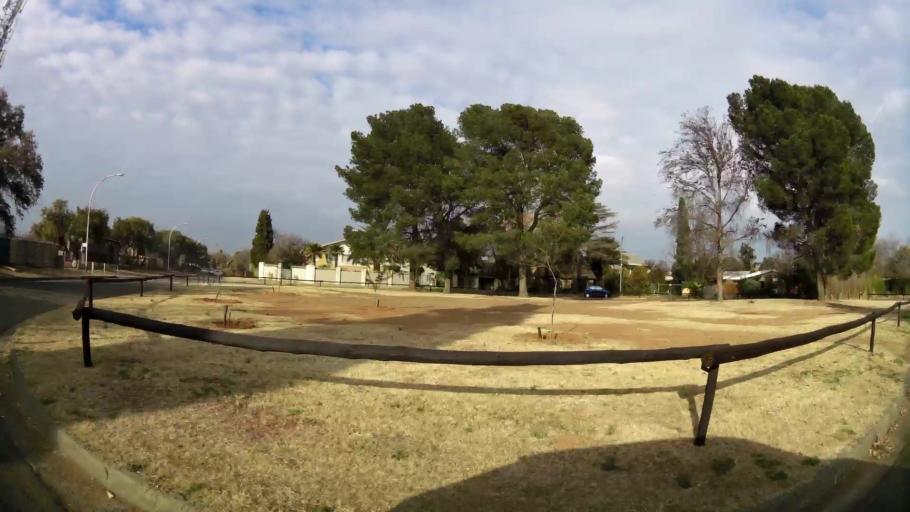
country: ZA
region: Orange Free State
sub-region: Mangaung Metropolitan Municipality
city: Bloemfontein
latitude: -29.1200
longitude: 26.1778
